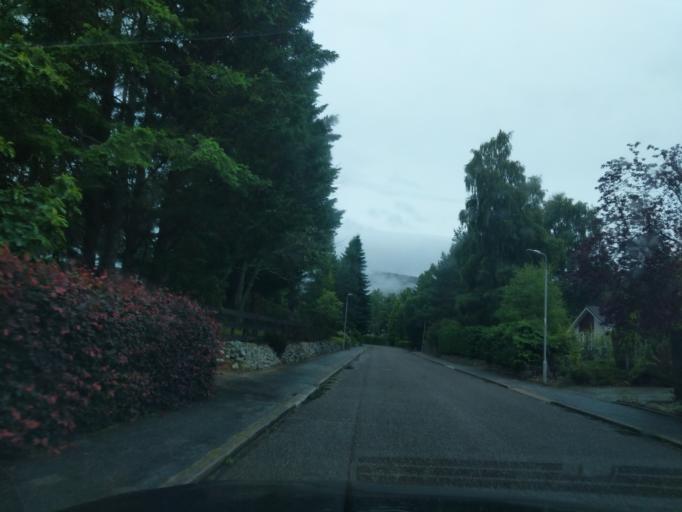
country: GB
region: Scotland
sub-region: Aberdeenshire
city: Aboyne
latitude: 57.0737
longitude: -2.7997
